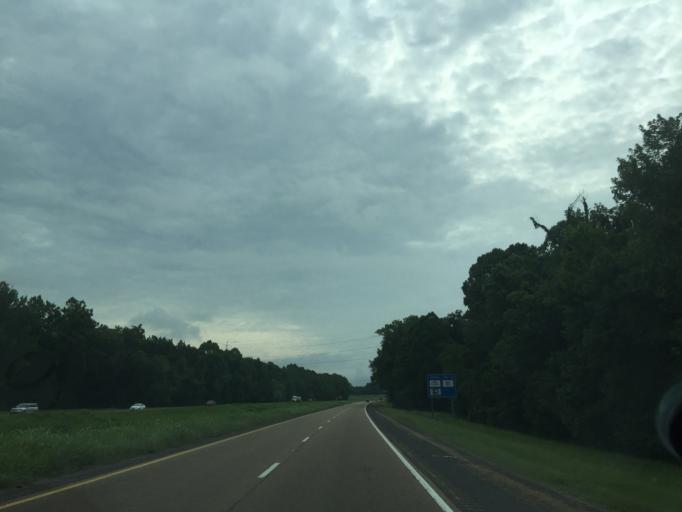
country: US
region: Mississippi
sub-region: Rankin County
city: Brandon
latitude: 32.2800
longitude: -90.0214
